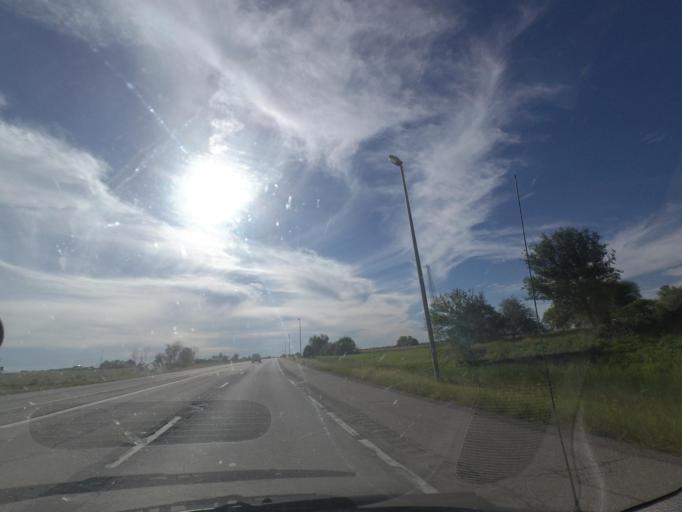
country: US
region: Illinois
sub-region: Macon County
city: Harristown
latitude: 39.8377
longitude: -89.0529
